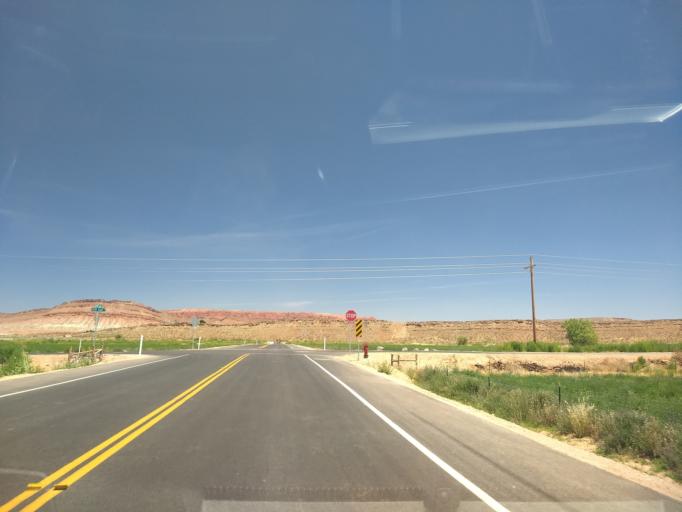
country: US
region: Utah
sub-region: Washington County
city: Washington
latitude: 37.0669
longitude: -113.5136
